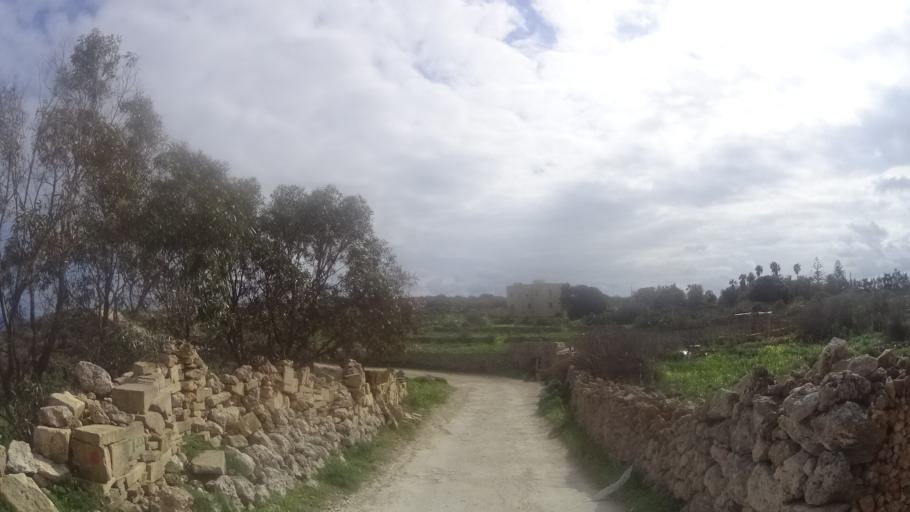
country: MT
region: Il-Qala
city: Qala
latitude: 36.0417
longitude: 14.3181
